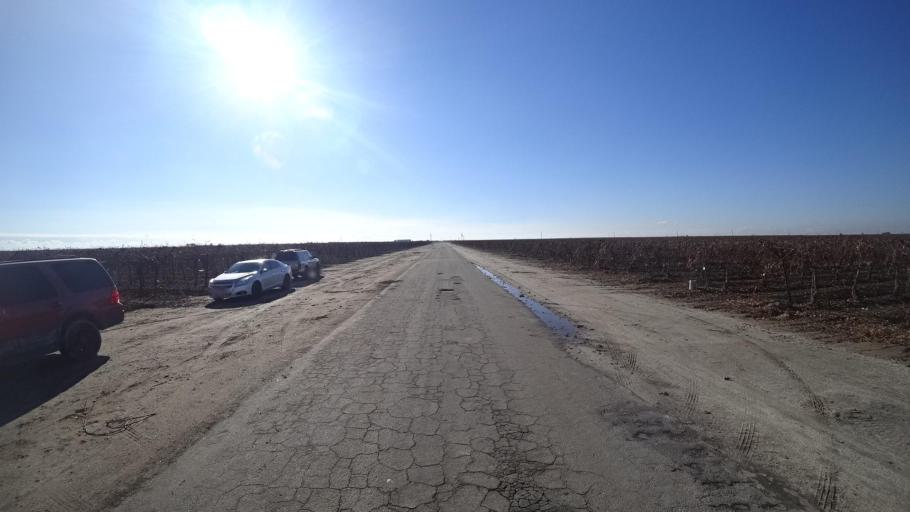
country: US
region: California
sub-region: Kern County
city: Delano
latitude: 35.7215
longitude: -119.2853
